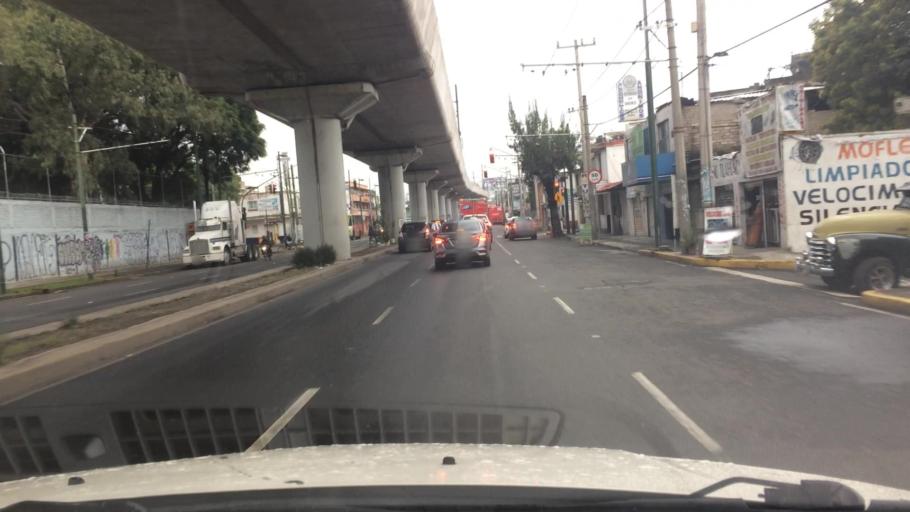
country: MX
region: Mexico City
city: Iztapalapa
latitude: 19.3332
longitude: -99.1084
